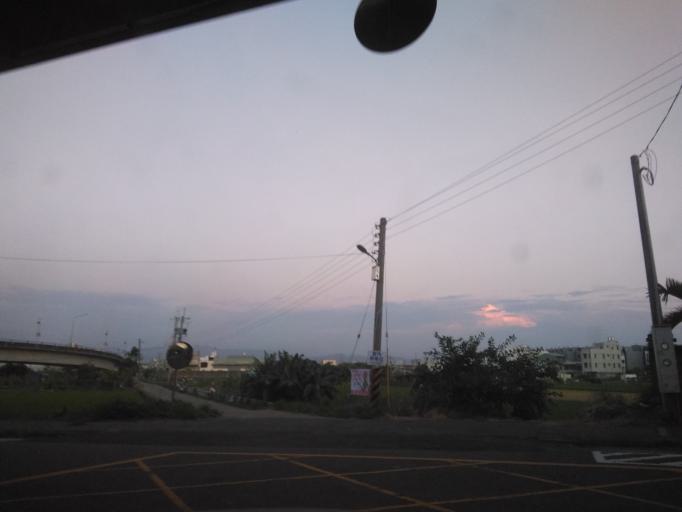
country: TW
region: Taiwan
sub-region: Changhua
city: Chang-hua
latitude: 24.0845
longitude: 120.5961
